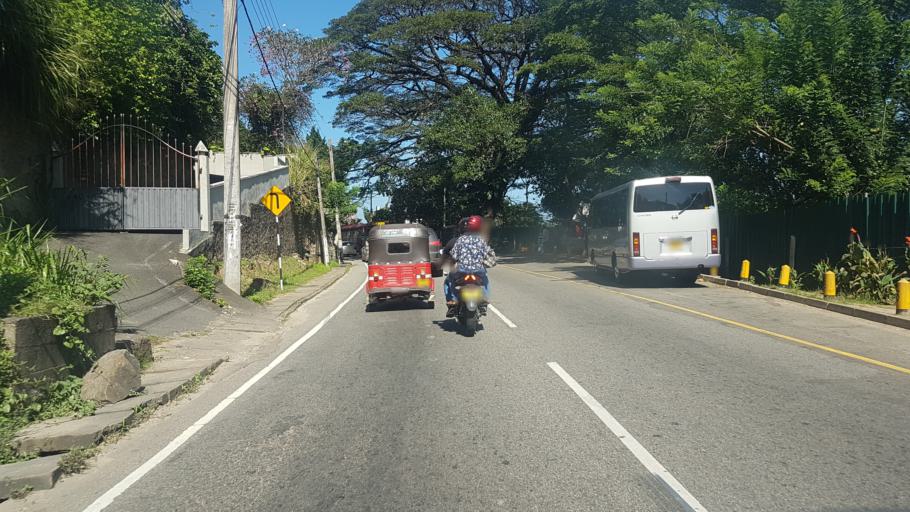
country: LK
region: Central
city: Kandy
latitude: 7.2936
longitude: 80.6528
